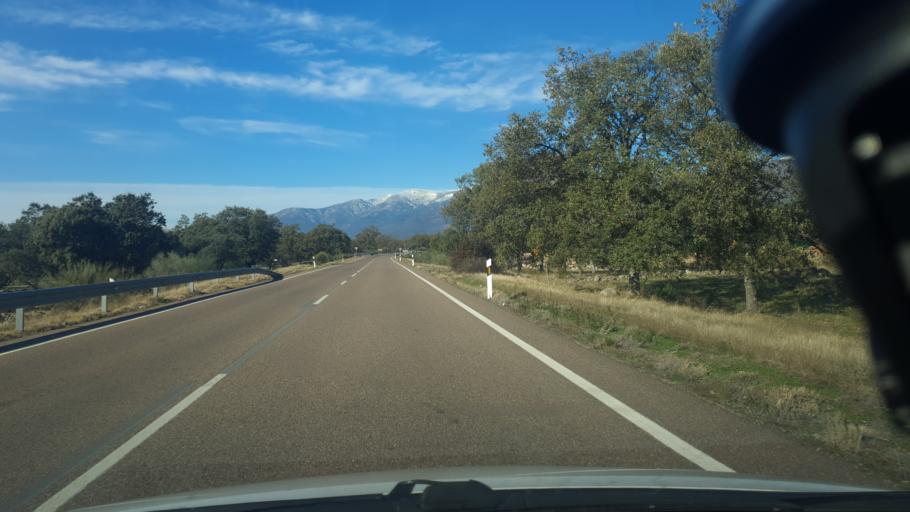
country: ES
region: Castille and Leon
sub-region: Provincia de Avila
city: Candeleda
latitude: 40.1399
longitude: -5.2558
